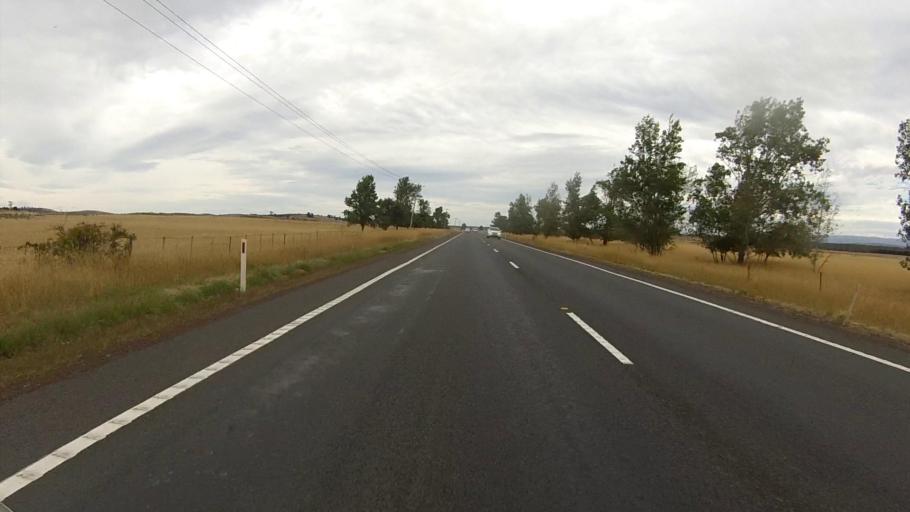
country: AU
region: Tasmania
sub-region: Northern Midlands
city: Evandale
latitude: -41.8912
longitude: 147.4708
